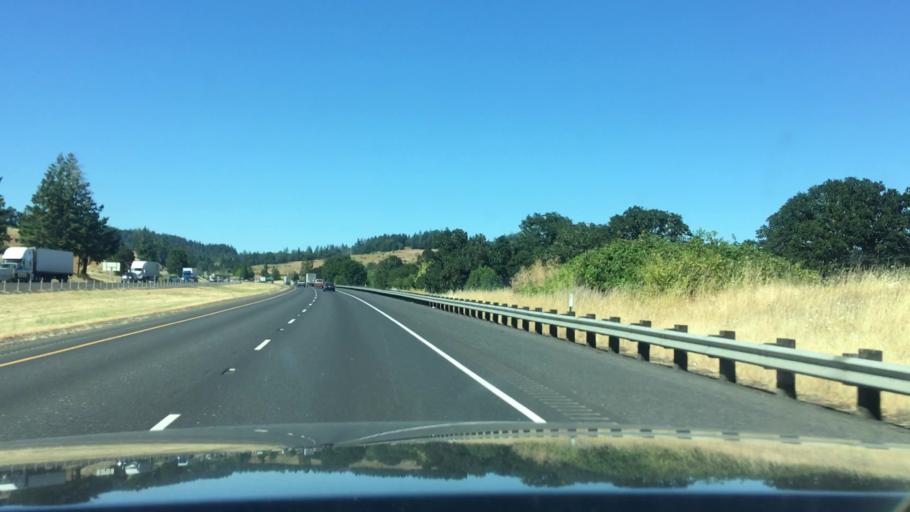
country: US
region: Oregon
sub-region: Douglas County
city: Yoncalla
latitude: 43.5034
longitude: -123.3199
